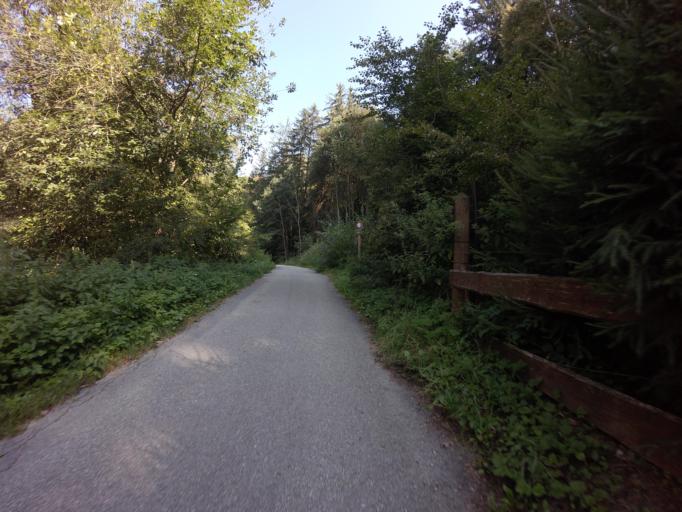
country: CZ
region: Jihocesky
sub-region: Okres Cesky Krumlov
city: Cesky Krumlov
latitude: 48.8567
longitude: 14.3740
